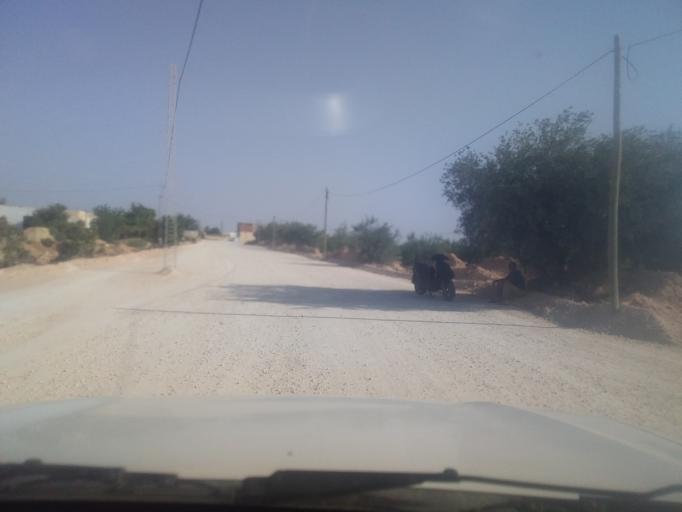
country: TN
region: Qabis
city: Matmata
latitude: 33.5975
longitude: 10.2734
